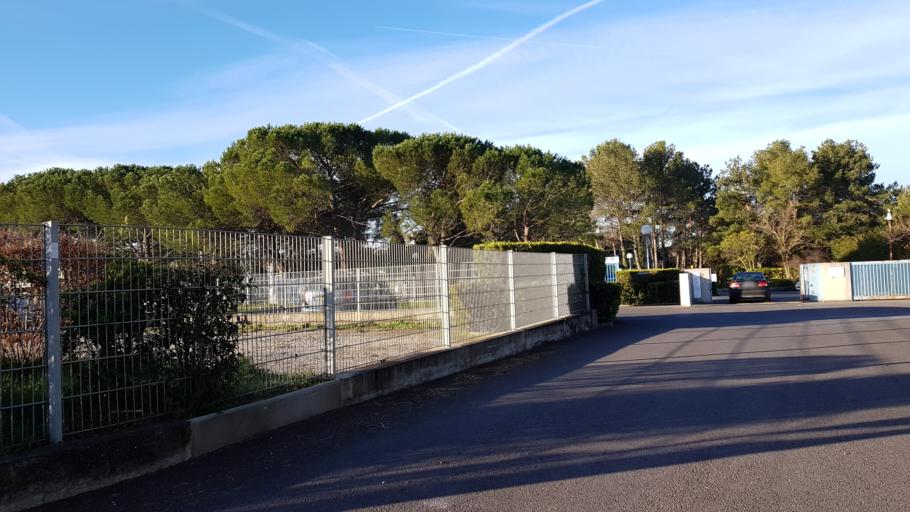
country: FR
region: Provence-Alpes-Cote d'Azur
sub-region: Departement des Bouches-du-Rhone
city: Cabries
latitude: 43.4925
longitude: 5.3785
